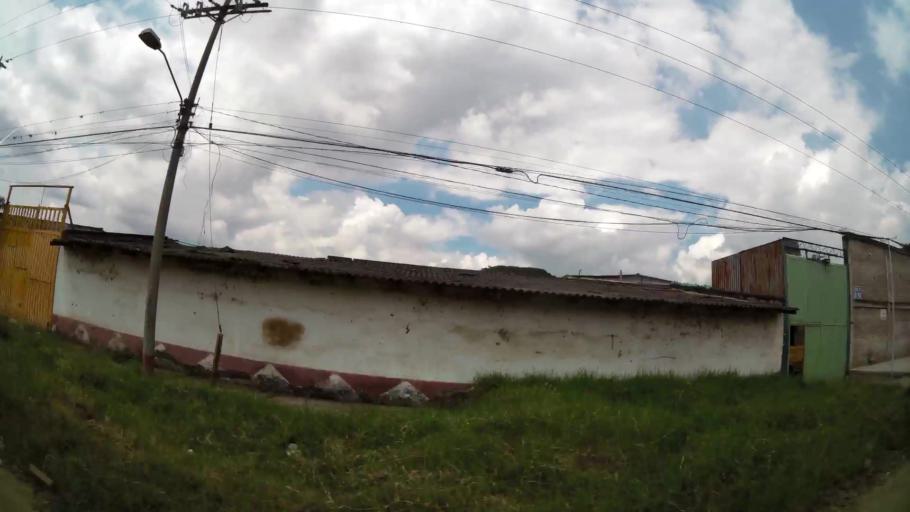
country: CO
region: Valle del Cauca
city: Cali
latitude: 3.4990
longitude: -76.4790
